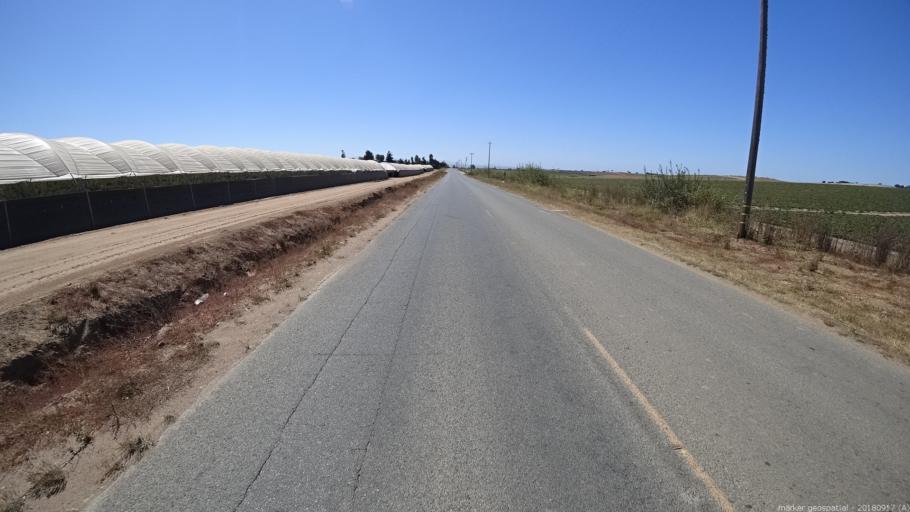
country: US
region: California
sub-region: Monterey County
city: Prunedale
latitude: 36.7654
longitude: -121.6108
